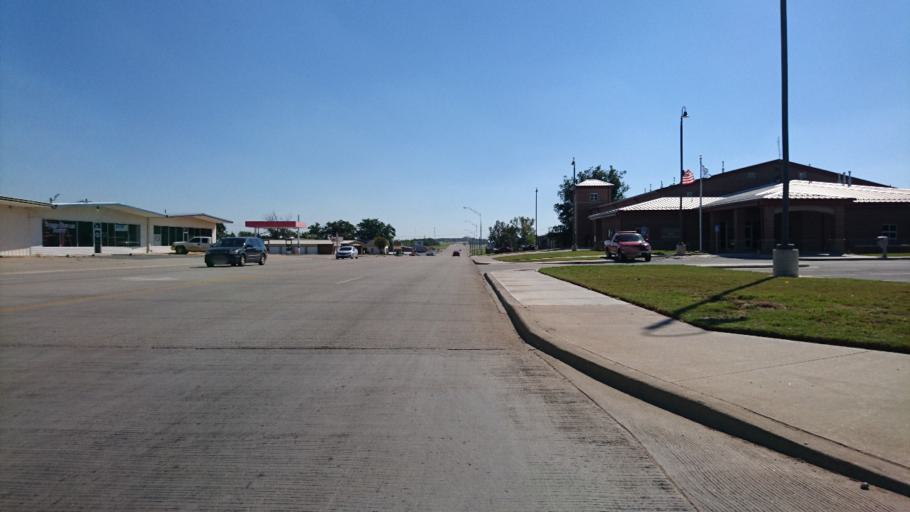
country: US
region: Oklahoma
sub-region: Custer County
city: Clinton
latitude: 35.5133
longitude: -98.9649
